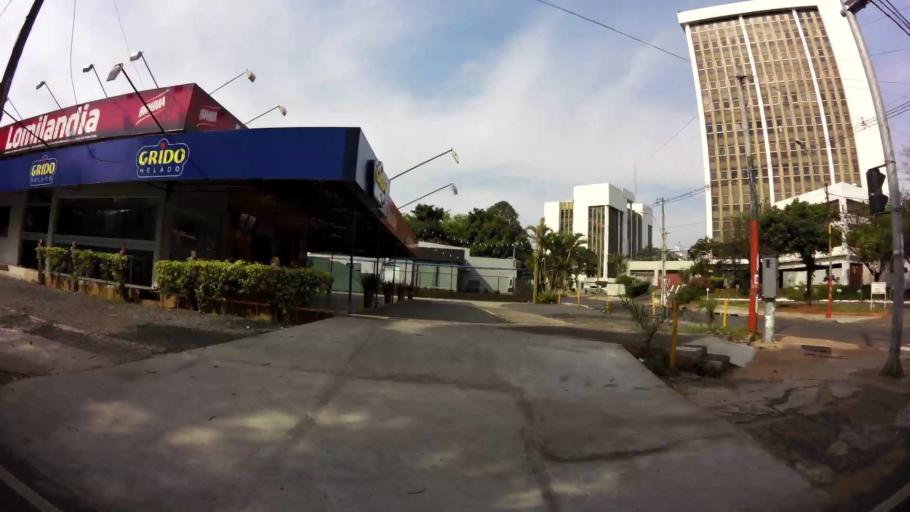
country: PY
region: Central
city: Fernando de la Mora
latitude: -25.3042
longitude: -57.5591
